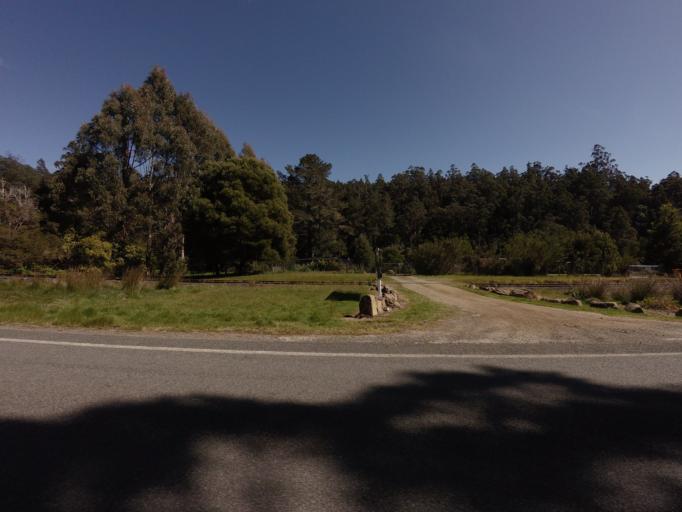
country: AU
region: Tasmania
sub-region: Derwent Valley
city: New Norfolk
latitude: -42.7200
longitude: 146.6835
